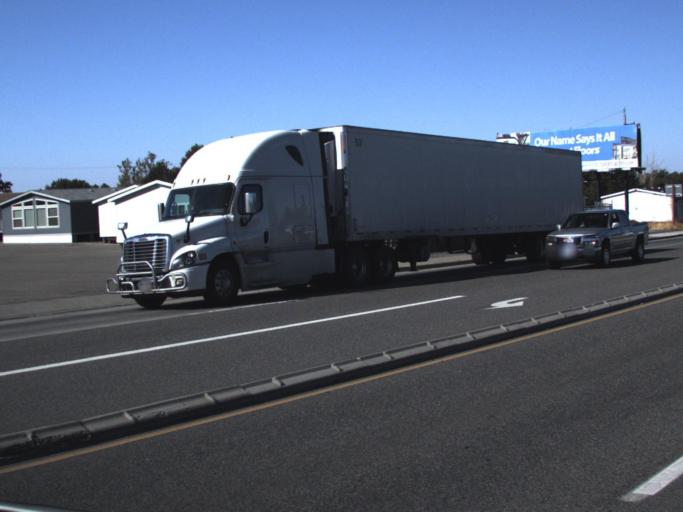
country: US
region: Washington
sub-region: Benton County
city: Kennewick
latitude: 46.2001
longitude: -119.1588
